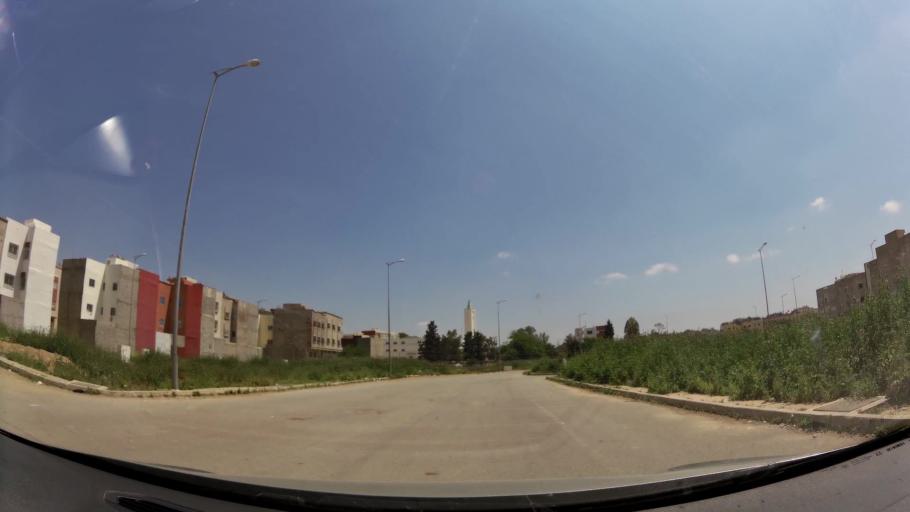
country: MA
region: Fes-Boulemane
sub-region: Fes
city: Fes
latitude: 34.0203
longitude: -5.0589
